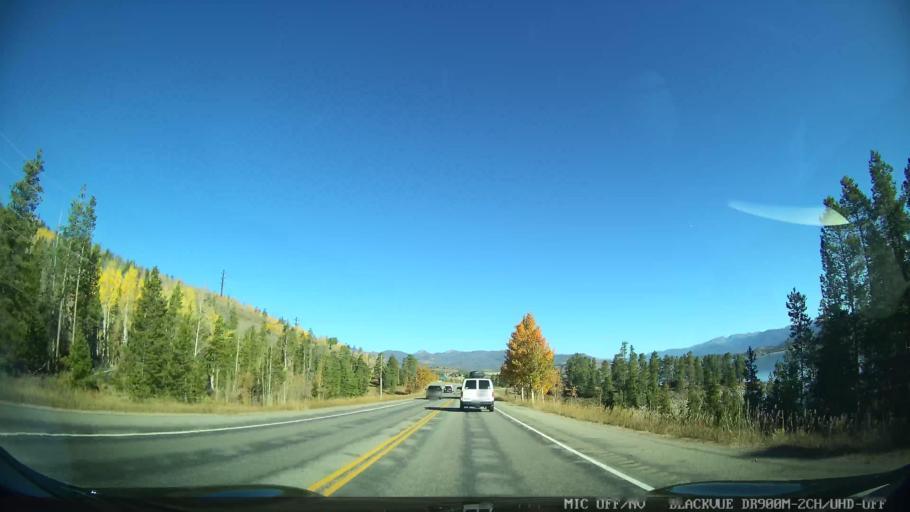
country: US
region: Colorado
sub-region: Grand County
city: Granby
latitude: 40.1548
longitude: -105.8896
